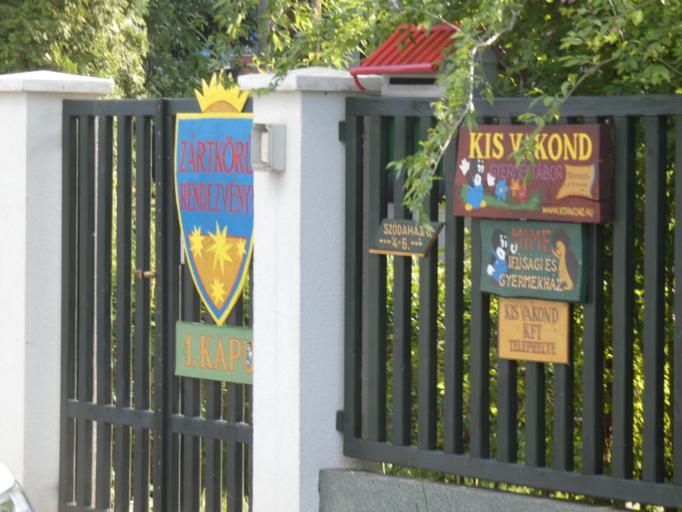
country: HU
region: Szabolcs-Szatmar-Bereg
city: Kotaj
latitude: 48.0058
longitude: 21.7309
